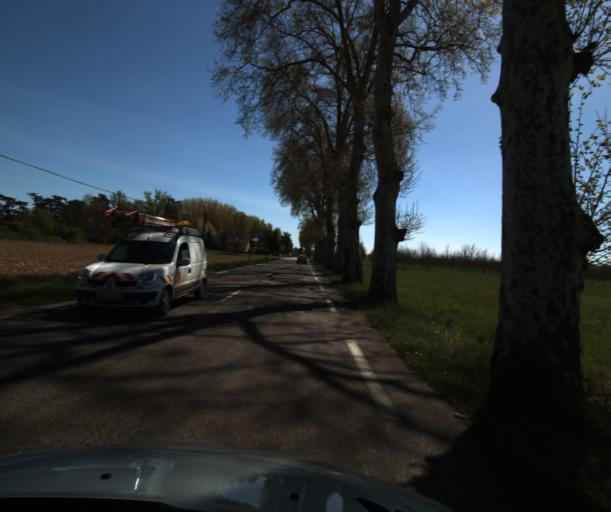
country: FR
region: Midi-Pyrenees
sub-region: Departement du Tarn-et-Garonne
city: Montbeton
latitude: 44.0771
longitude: 1.2816
